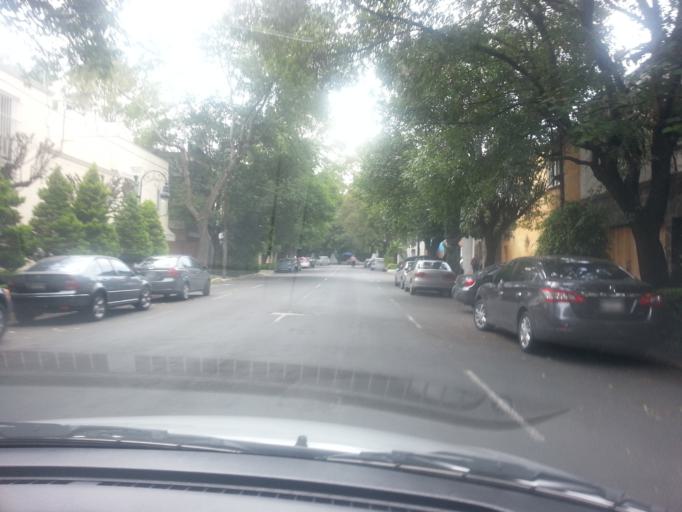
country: MX
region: Mexico City
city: Coyoacan
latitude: 19.3518
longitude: -99.1682
